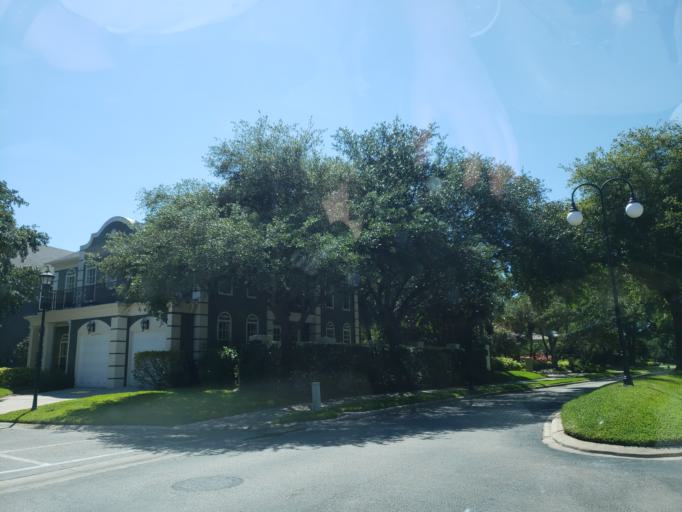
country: US
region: Florida
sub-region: Hillsborough County
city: Tampa
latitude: 27.9350
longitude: -82.4512
